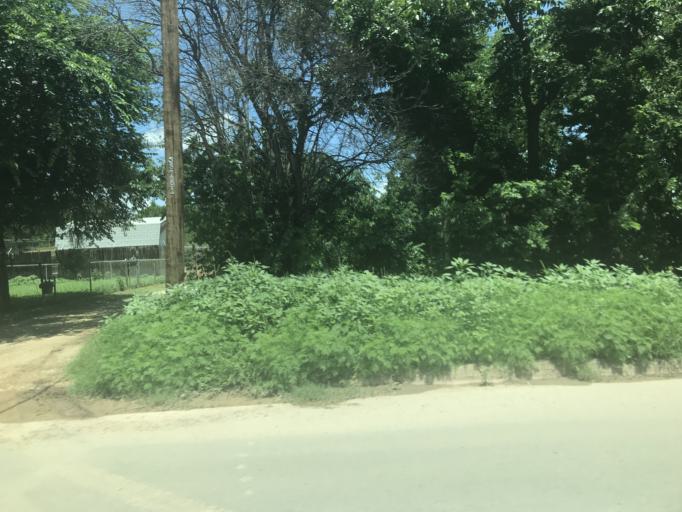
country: US
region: Texas
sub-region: Taylor County
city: Abilene
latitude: 32.4671
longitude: -99.7526
